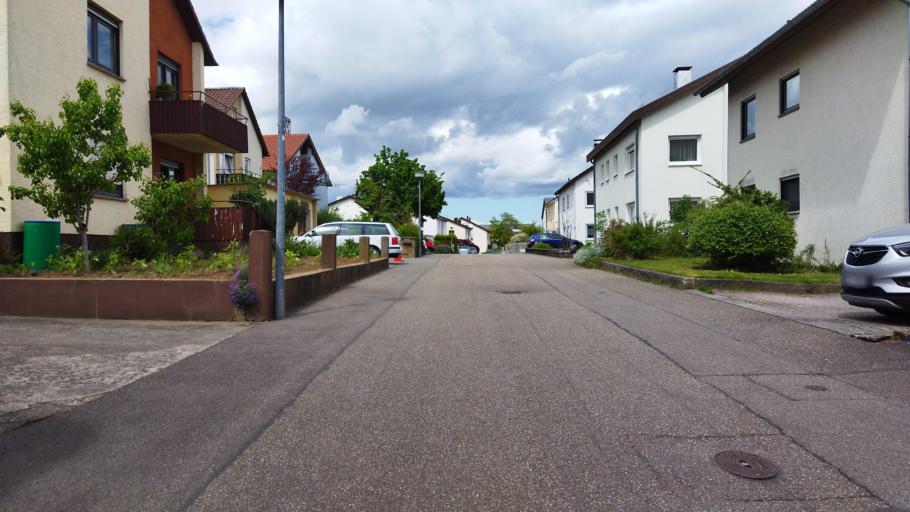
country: DE
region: Baden-Wuerttemberg
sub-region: Regierungsbezirk Stuttgart
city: Leingarten
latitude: 49.1831
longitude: 9.1215
